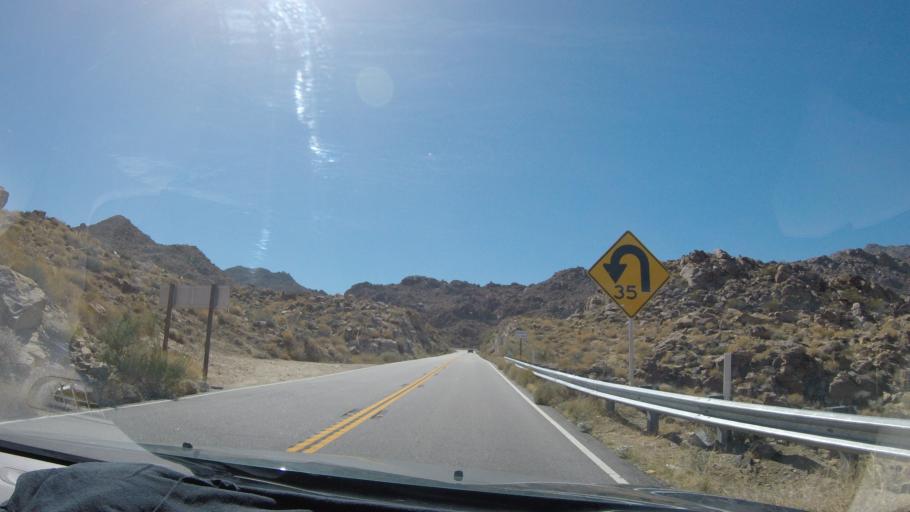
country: US
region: California
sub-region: Riverside County
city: Palm Desert
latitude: 33.6487
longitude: -116.4063
